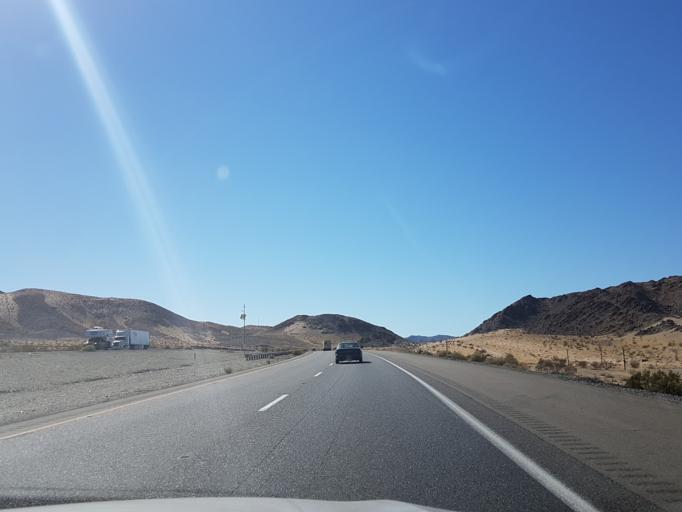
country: US
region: California
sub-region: San Bernardino County
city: Fort Irwin
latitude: 35.0830
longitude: -116.3799
